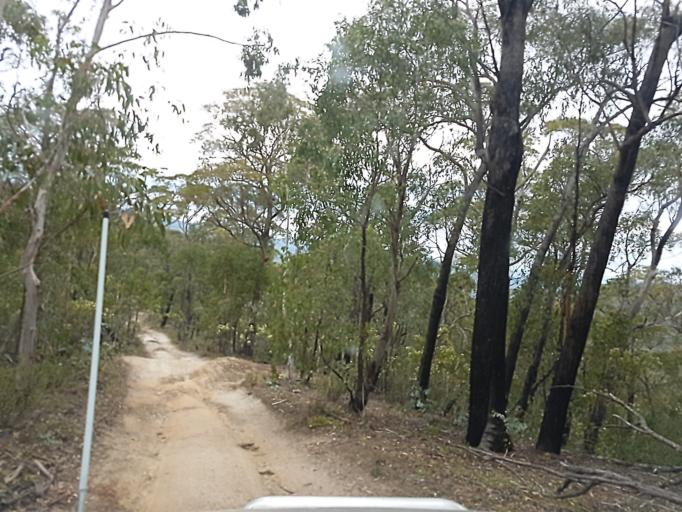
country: AU
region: New South Wales
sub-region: Snowy River
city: Jindabyne
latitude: -36.8707
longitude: 148.2763
